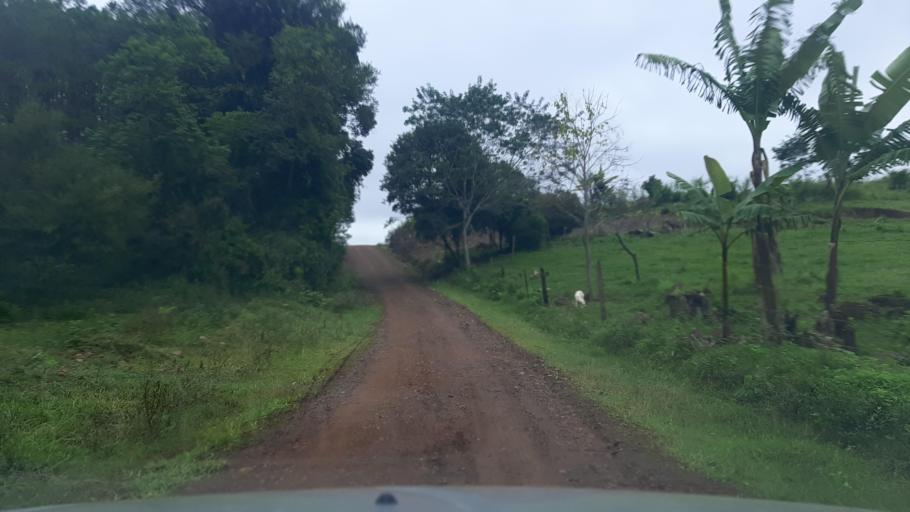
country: BR
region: Parana
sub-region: Ampere
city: Ampere
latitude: -26.0572
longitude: -53.5519
